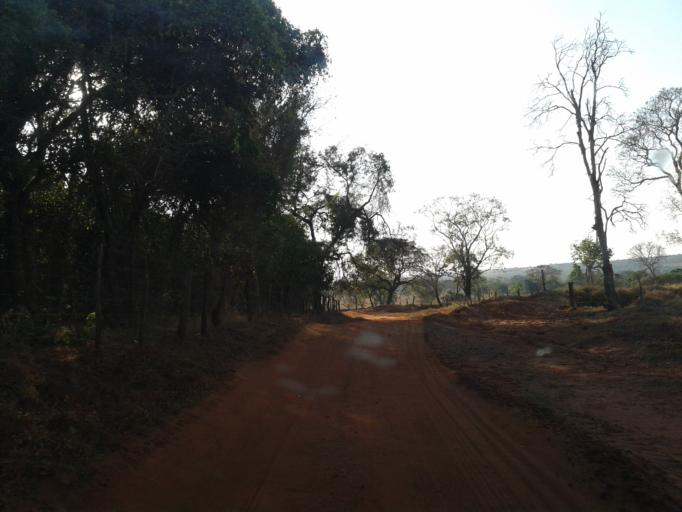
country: BR
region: Minas Gerais
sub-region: Ituiutaba
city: Ituiutaba
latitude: -19.2435
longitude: -49.5922
